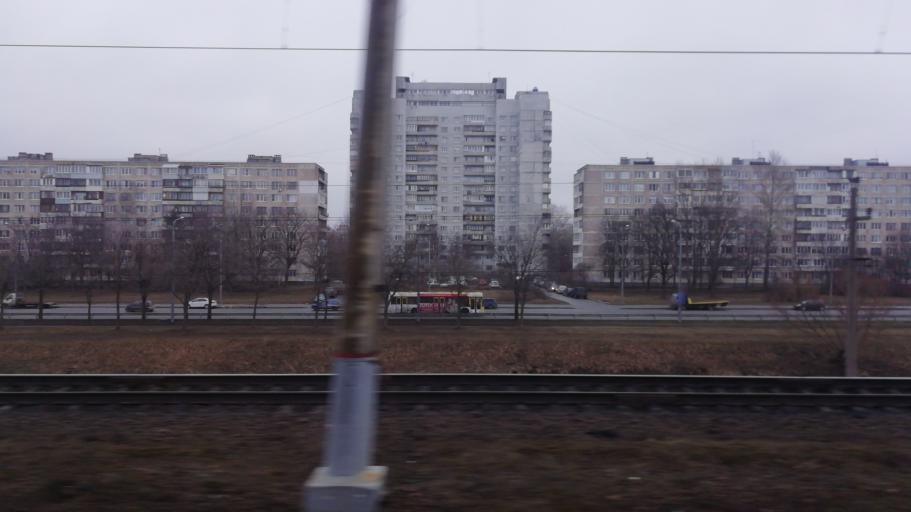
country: RU
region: St.-Petersburg
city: Kupchino
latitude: 59.8692
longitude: 30.3568
